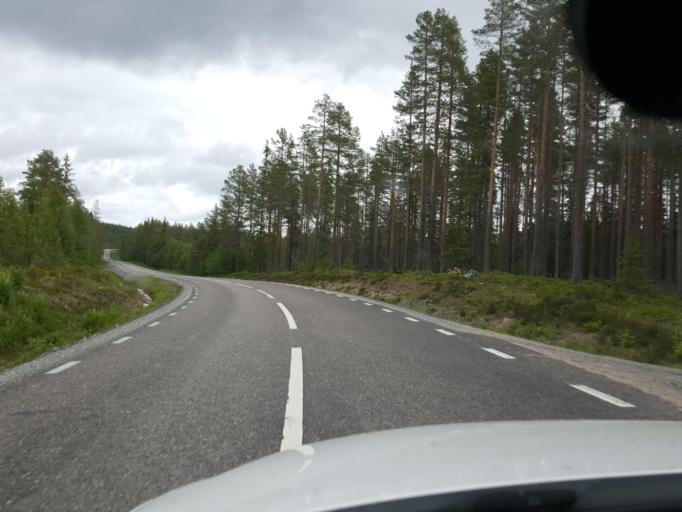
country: SE
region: Gaevleborg
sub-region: Ljusdals Kommun
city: Farila
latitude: 61.7539
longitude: 15.4479
